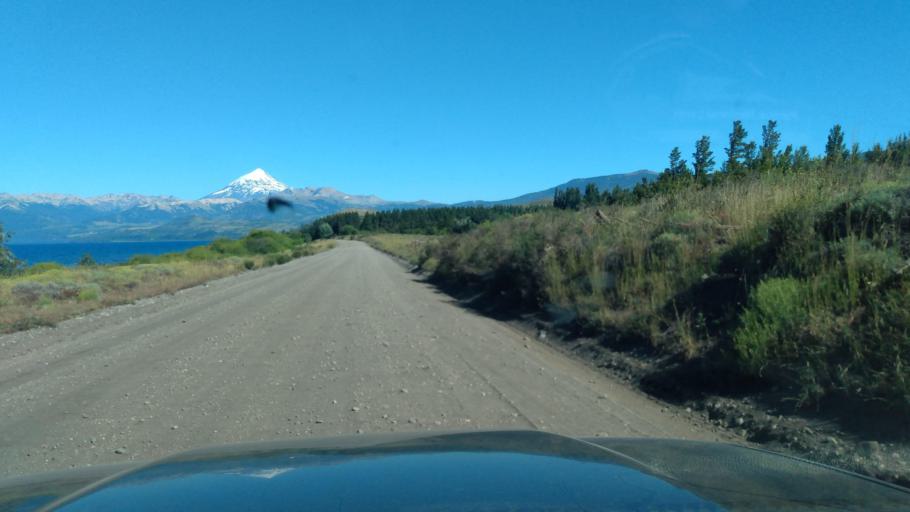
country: AR
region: Neuquen
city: Junin de los Andes
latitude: -39.7888
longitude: -71.2198
